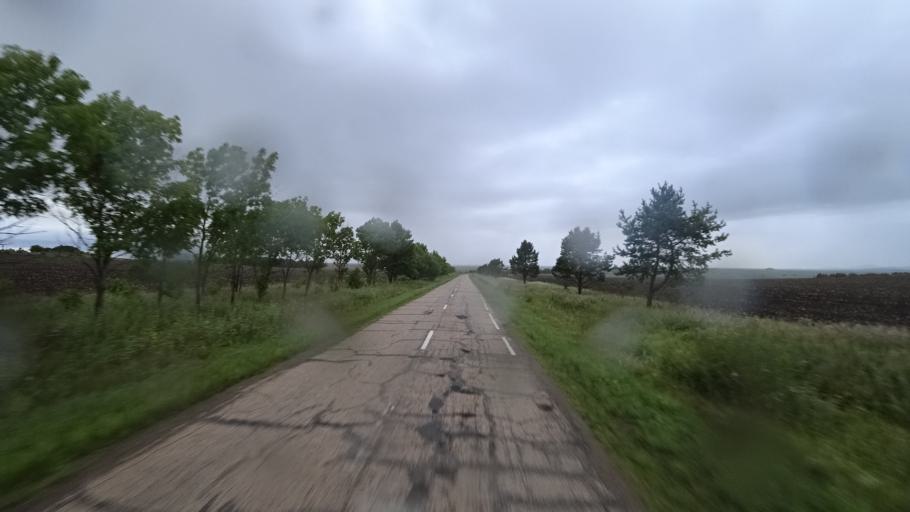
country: RU
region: Primorskiy
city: Chernigovka
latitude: 44.3682
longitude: 132.5329
